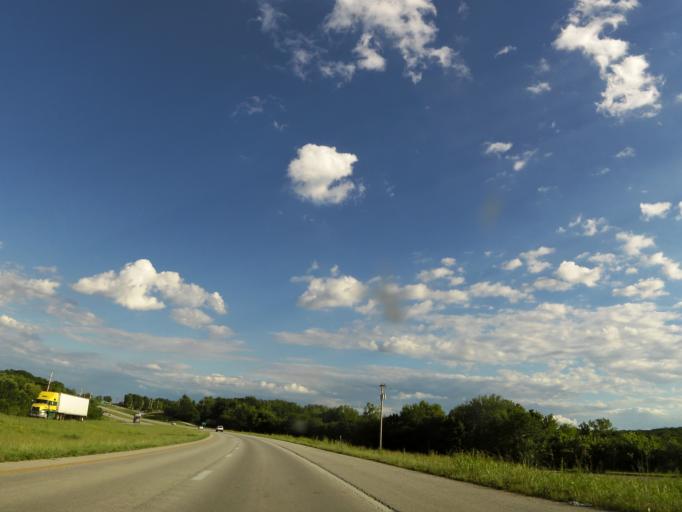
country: US
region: Missouri
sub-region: Lincoln County
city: Troy
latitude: 39.0076
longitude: -90.9780
